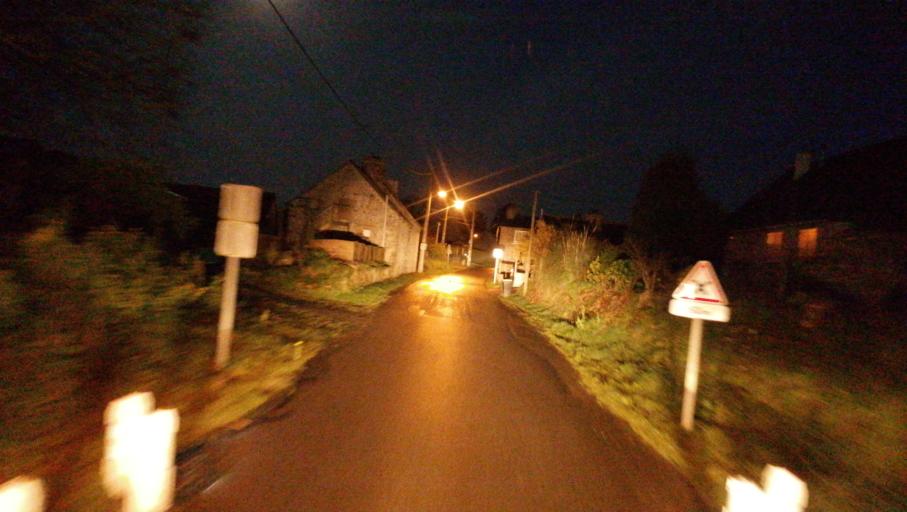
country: FR
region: Brittany
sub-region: Departement des Cotes-d'Armor
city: Plouha
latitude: 48.6719
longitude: -2.9483
